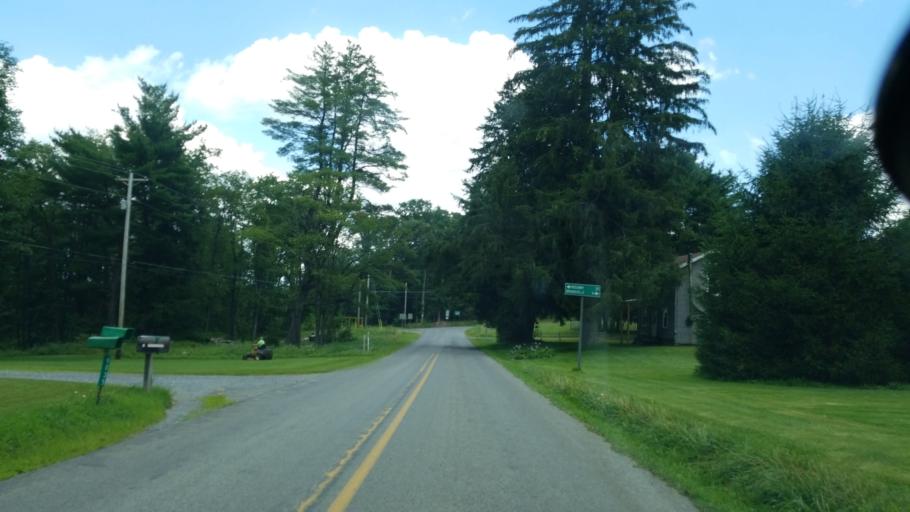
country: US
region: Pennsylvania
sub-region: Jefferson County
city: Brookville
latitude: 41.2396
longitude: -79.0138
